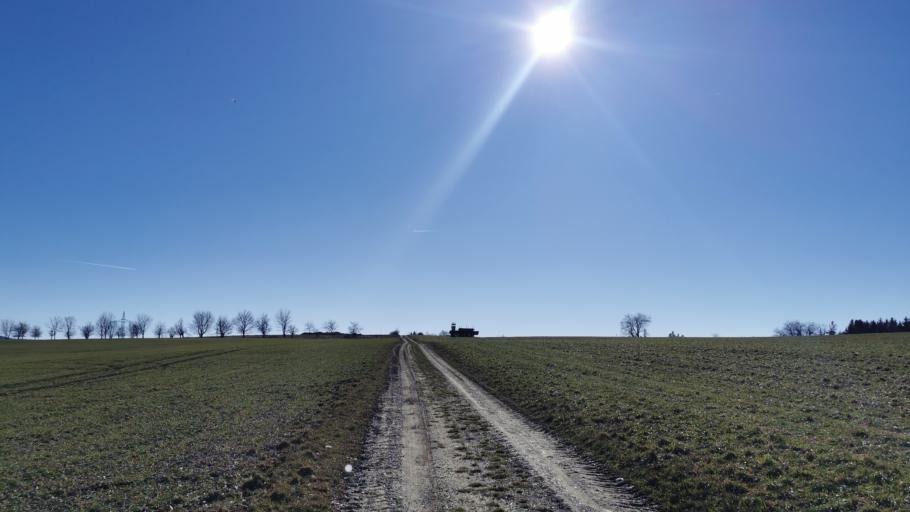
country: DE
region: Bavaria
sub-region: Upper Franconia
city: Ludwigsstadt
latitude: 50.4867
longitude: 11.4411
